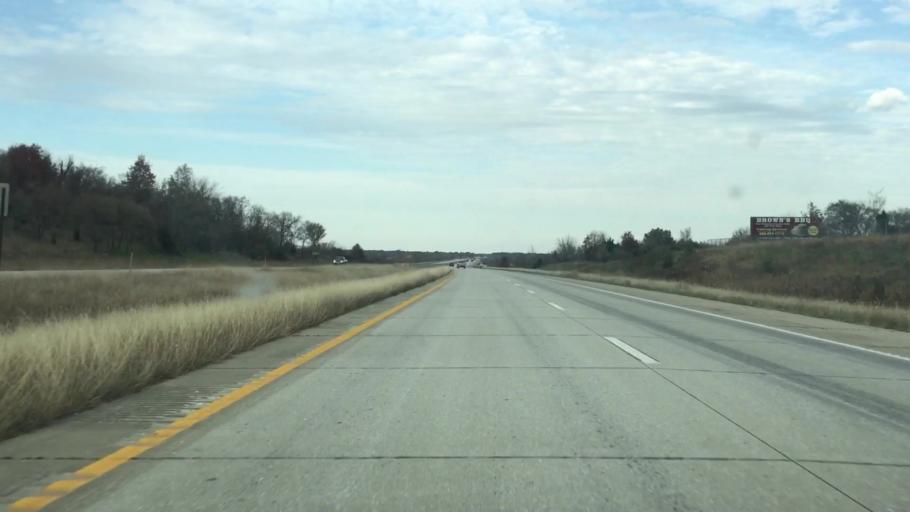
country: US
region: Missouri
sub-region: Henry County
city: Clinton
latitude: 38.3087
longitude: -93.7583
